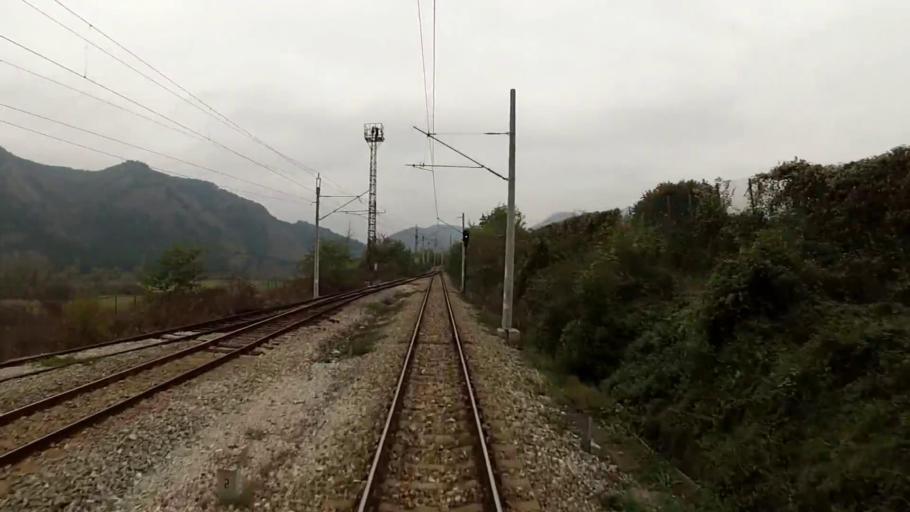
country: RS
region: Central Serbia
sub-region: Pirotski Okrug
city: Dimitrovgrad
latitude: 42.9895
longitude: 22.8516
